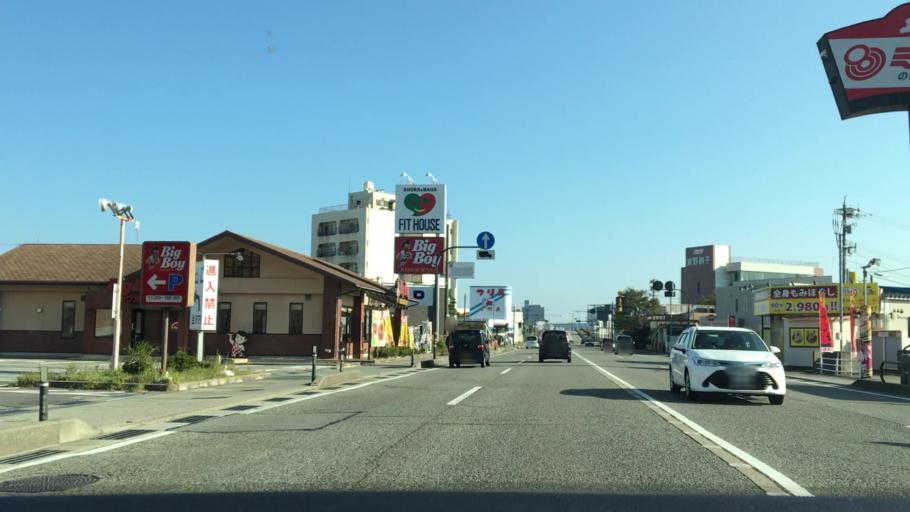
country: JP
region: Ishikawa
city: Nonoichi
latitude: 36.5374
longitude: 136.6185
